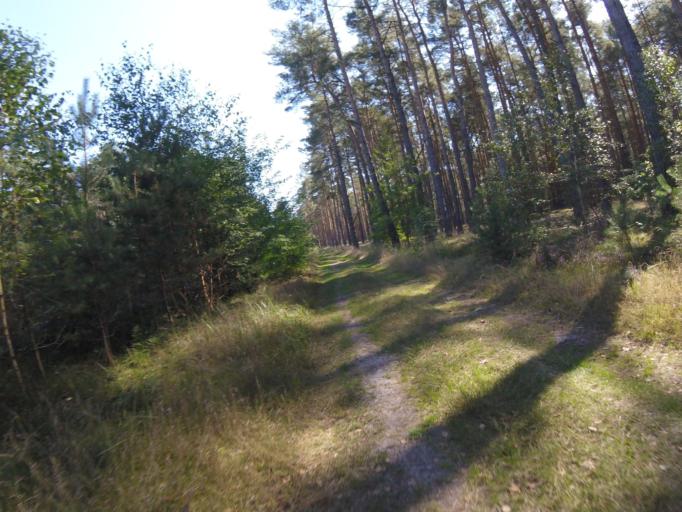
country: DE
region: Brandenburg
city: Bestensee
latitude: 52.2679
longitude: 13.6826
